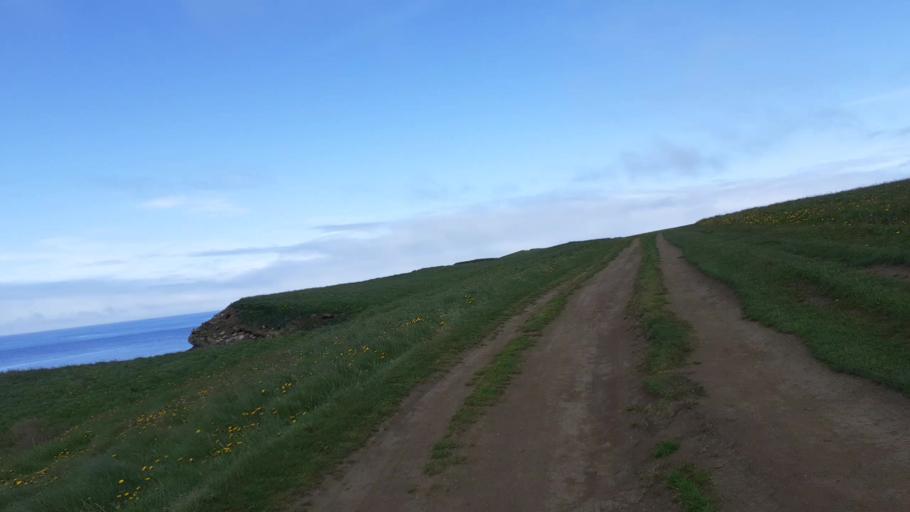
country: IS
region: Northeast
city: Dalvik
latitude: 66.5542
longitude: -18.0125
